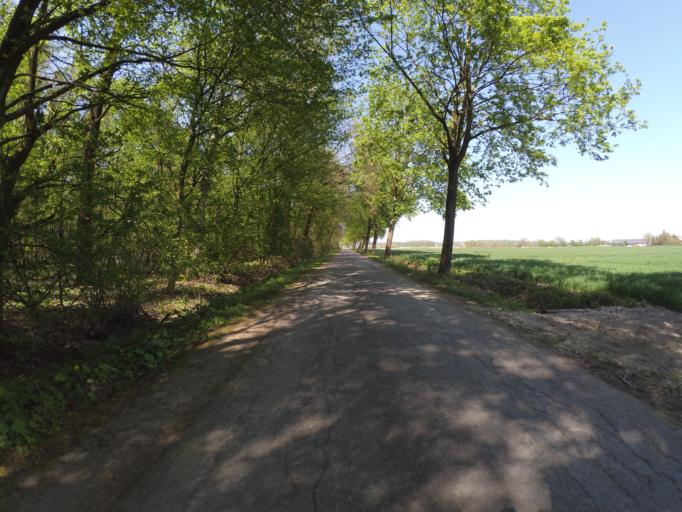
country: DE
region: North Rhine-Westphalia
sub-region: Regierungsbezirk Munster
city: Ascheberg
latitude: 51.8005
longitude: 7.6046
